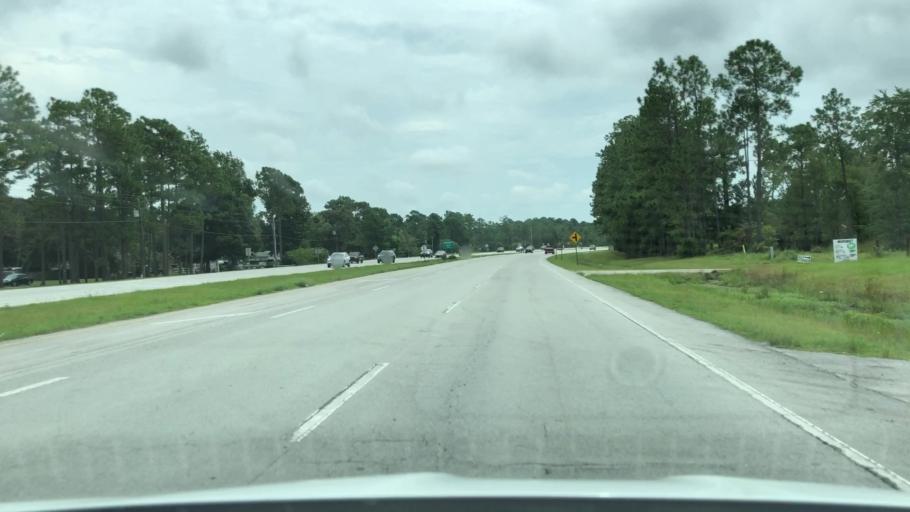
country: US
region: North Carolina
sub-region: Carteret County
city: Newport
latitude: 34.8282
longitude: -76.8774
